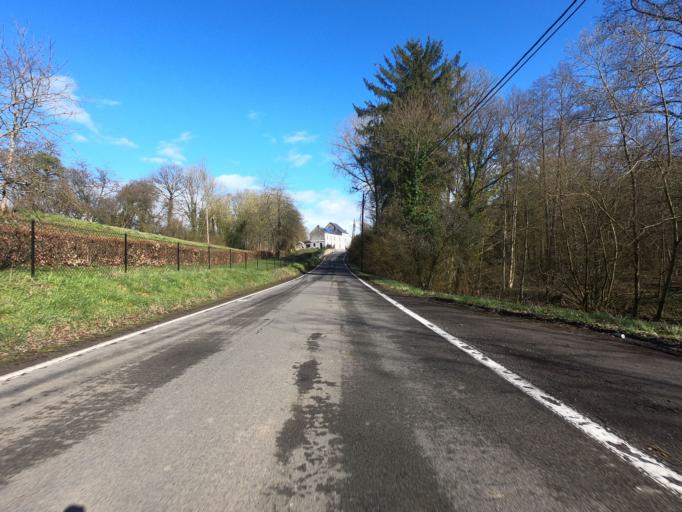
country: BE
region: Wallonia
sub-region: Province de Namur
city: Mettet
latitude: 50.3012
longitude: 4.7304
